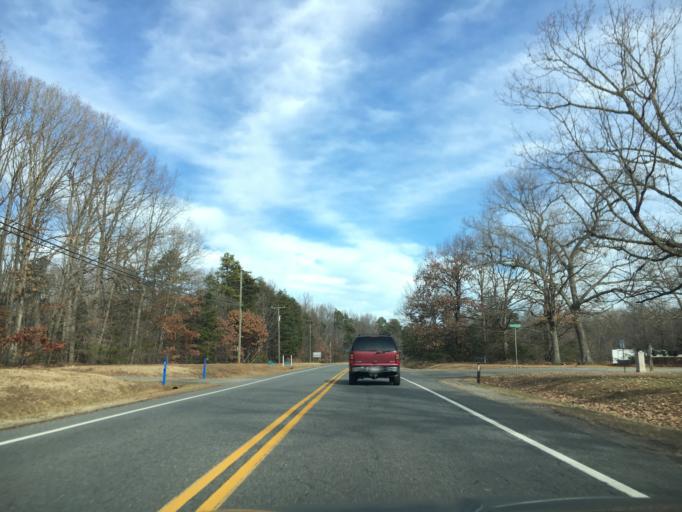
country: US
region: Virginia
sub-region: Louisa County
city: Louisa
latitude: 38.0210
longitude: -77.9022
